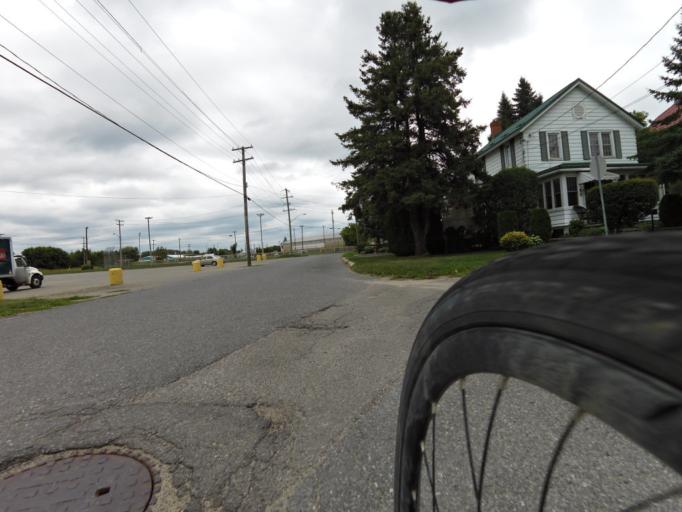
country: CA
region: Ontario
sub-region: Lanark County
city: Smiths Falls
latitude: 44.9035
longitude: -76.0269
